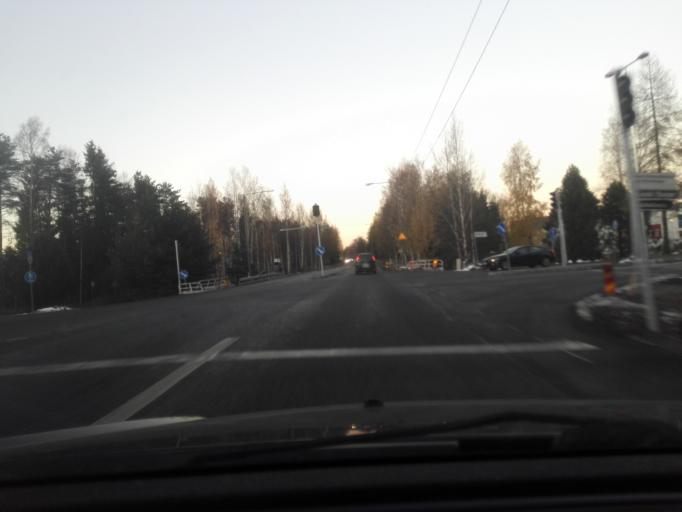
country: FI
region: Uusimaa
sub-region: Helsinki
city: Vantaa
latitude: 60.2969
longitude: 25.1019
